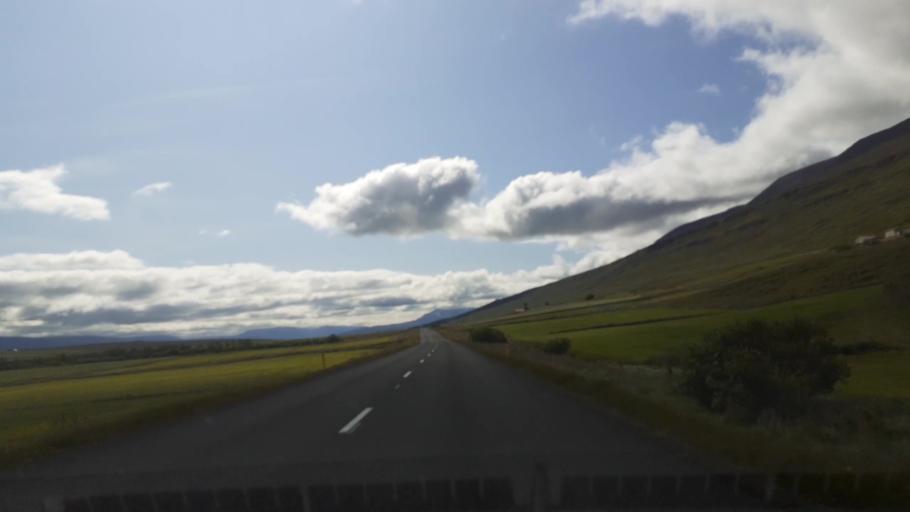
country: IS
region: Northeast
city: Akureyri
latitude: 65.8668
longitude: -18.2622
